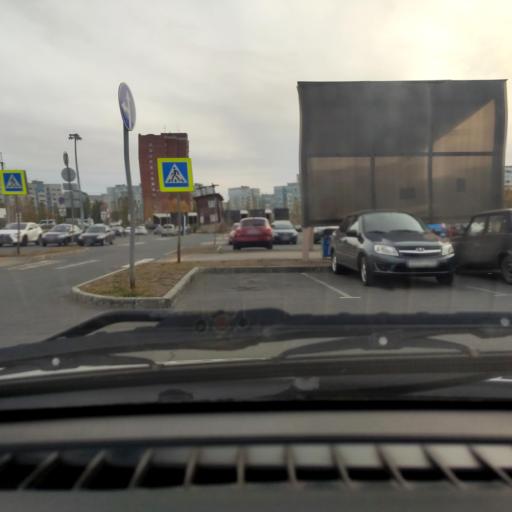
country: RU
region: Samara
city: Tol'yatti
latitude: 53.5501
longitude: 49.3435
